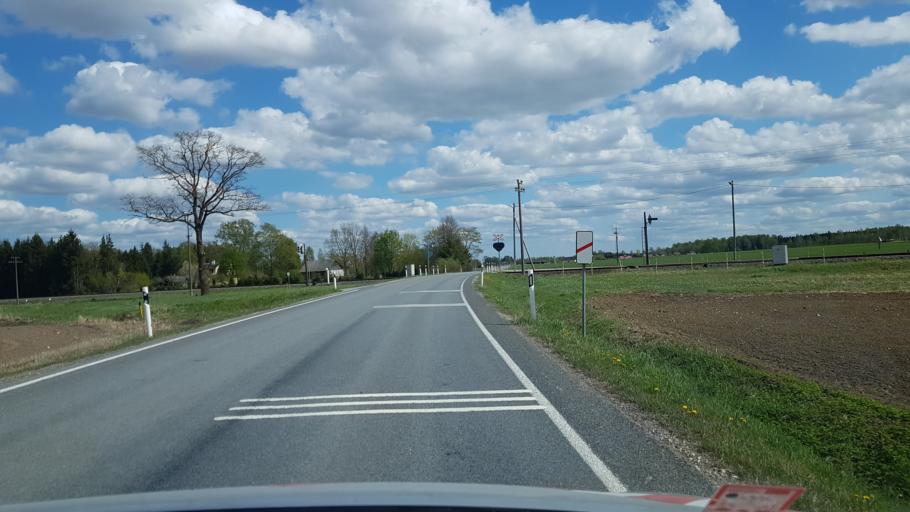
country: EE
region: Tartu
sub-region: UElenurme vald
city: Ulenurme
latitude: 58.3174
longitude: 26.6322
